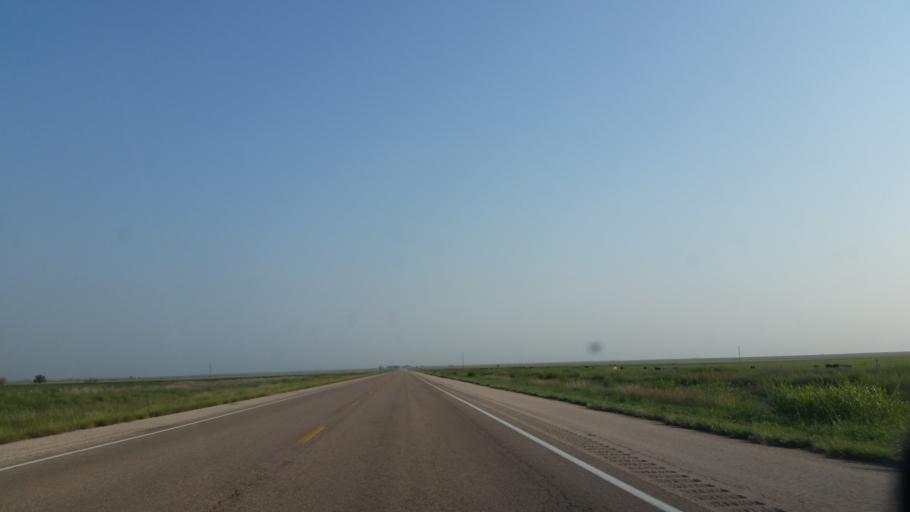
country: US
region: New Mexico
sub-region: Curry County
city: Clovis
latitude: 34.7738
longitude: -103.2144
